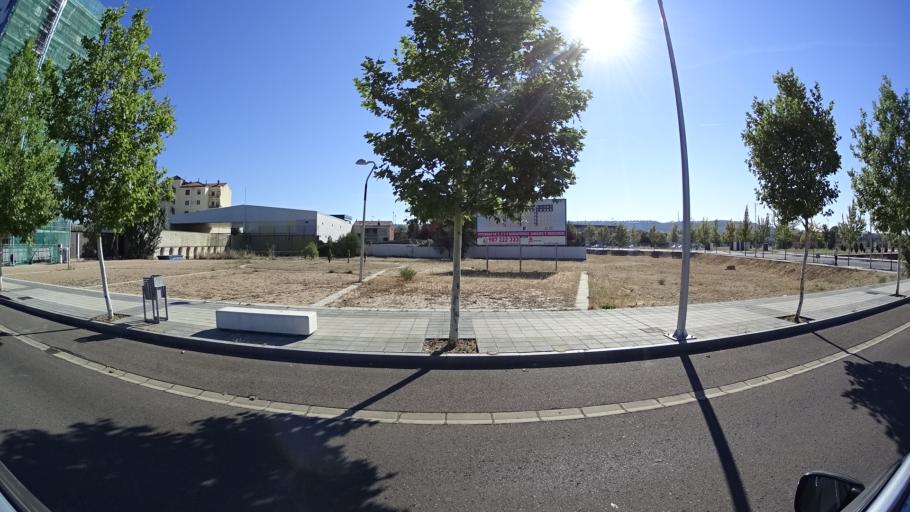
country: ES
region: Castille and Leon
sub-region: Provincia de Leon
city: Leon
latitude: 42.5849
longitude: -5.5605
